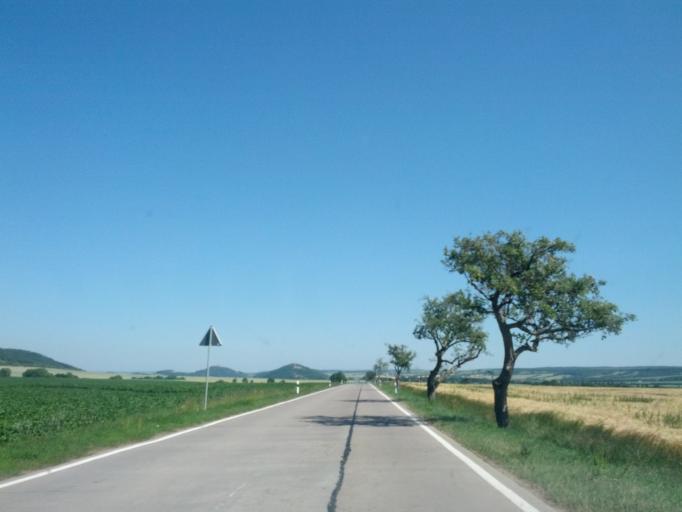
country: DE
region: Thuringia
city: Seebergen
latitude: 50.8898
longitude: 10.7856
